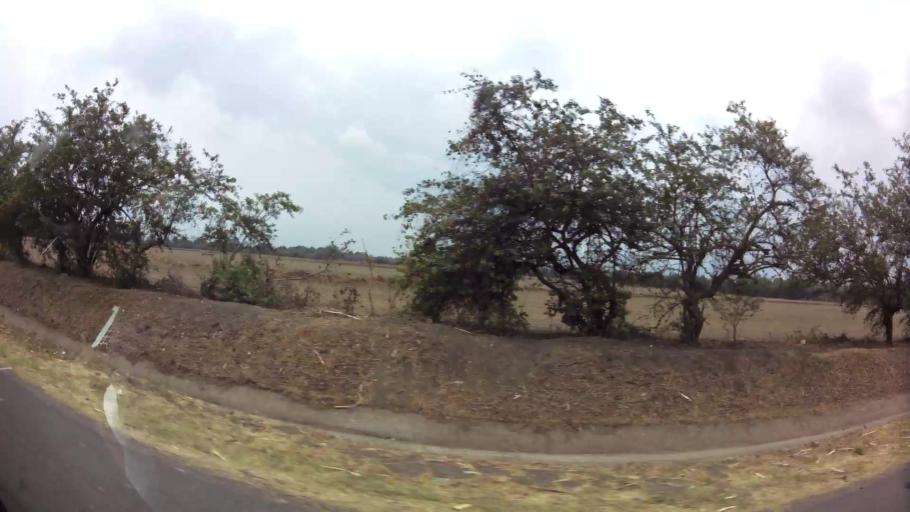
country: NI
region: Leon
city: Quezalguaque
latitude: 12.5449
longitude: -86.9220
